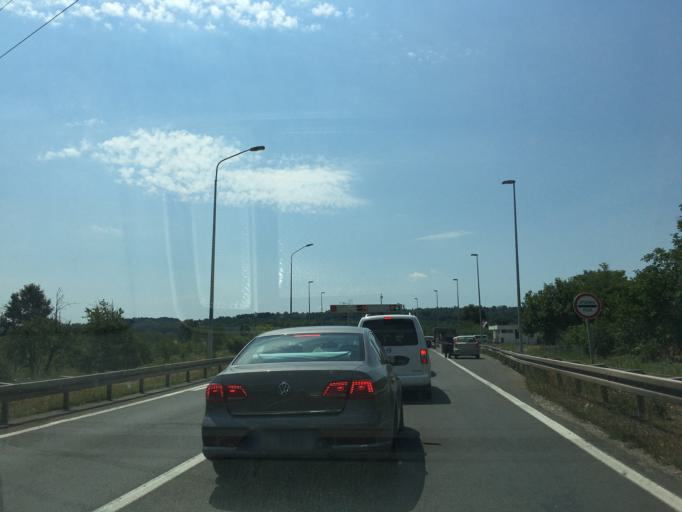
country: RS
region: Central Serbia
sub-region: Podunavski Okrug
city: Smederevo
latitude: 44.5908
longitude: 20.9571
